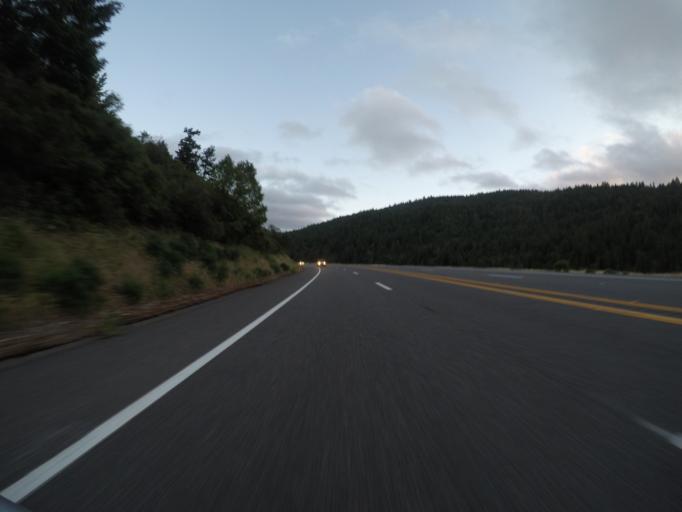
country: US
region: California
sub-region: Humboldt County
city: Redway
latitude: 40.0550
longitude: -123.7919
